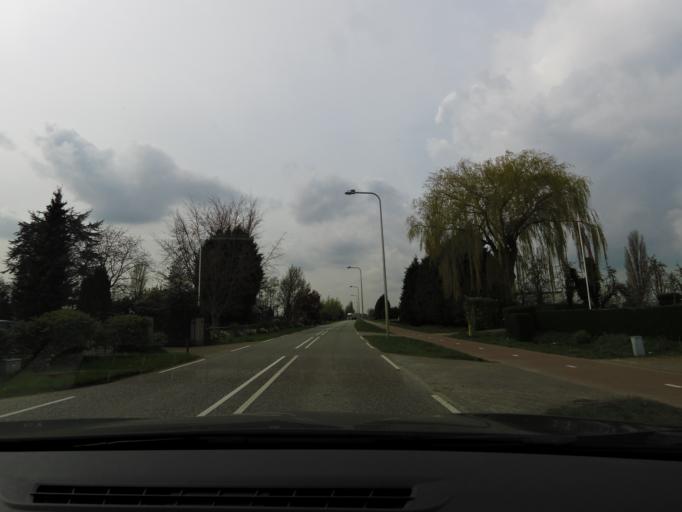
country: NL
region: South Holland
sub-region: Gemeente Albrandswaard
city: Rhoon
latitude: 51.8491
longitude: 4.4160
